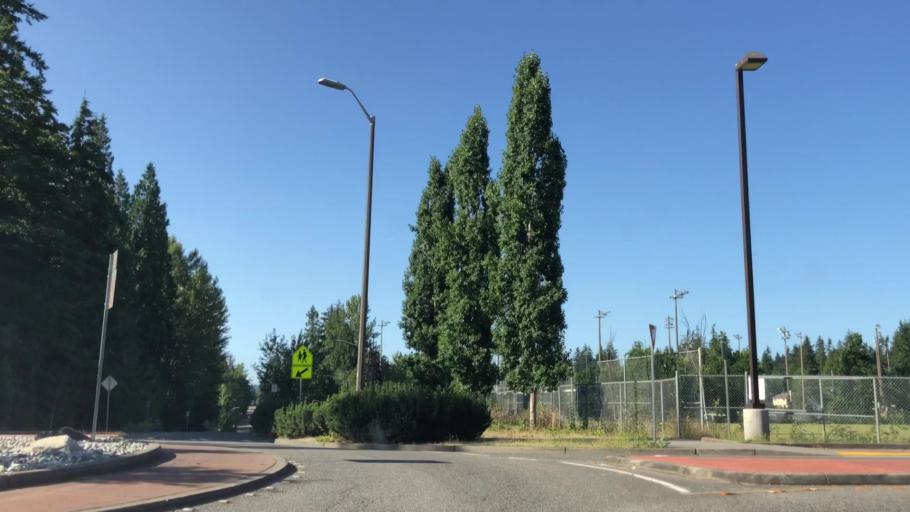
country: US
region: Washington
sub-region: King County
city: Woodinville
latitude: 47.7717
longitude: -122.1586
